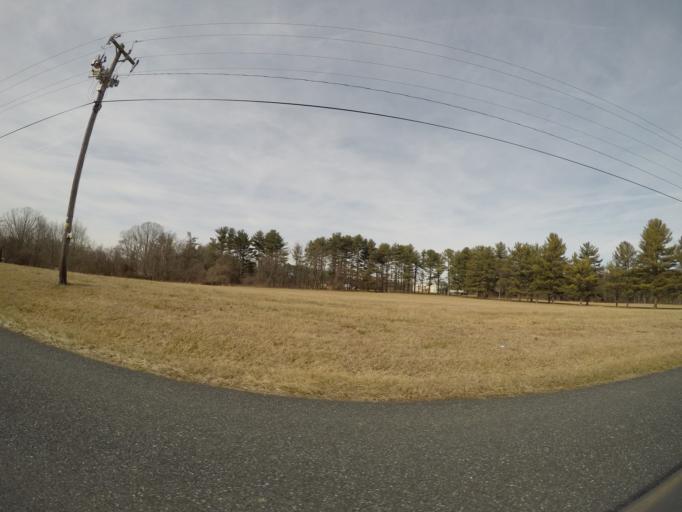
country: US
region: Maryland
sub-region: Cecil County
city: Rising Sun
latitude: 39.6649
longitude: -76.2140
